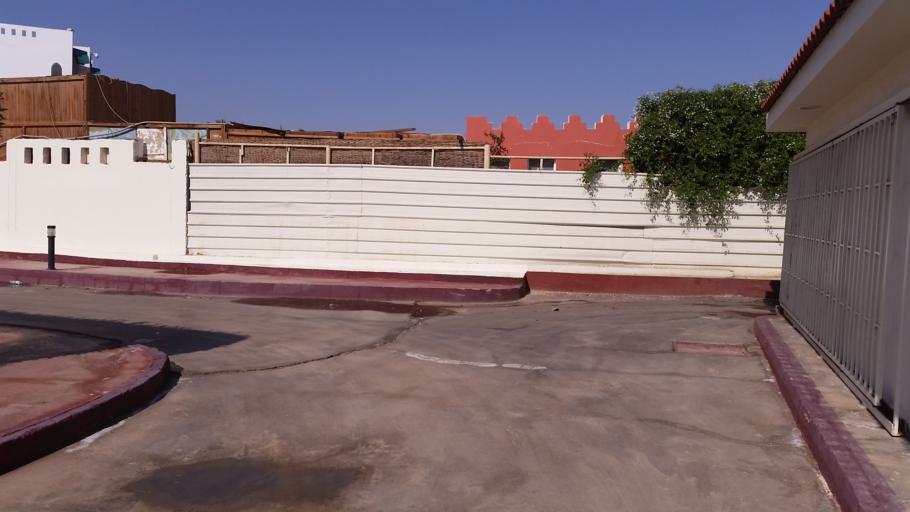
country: EG
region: Red Sea
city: Makadi Bay
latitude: 27.1013
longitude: 33.8338
